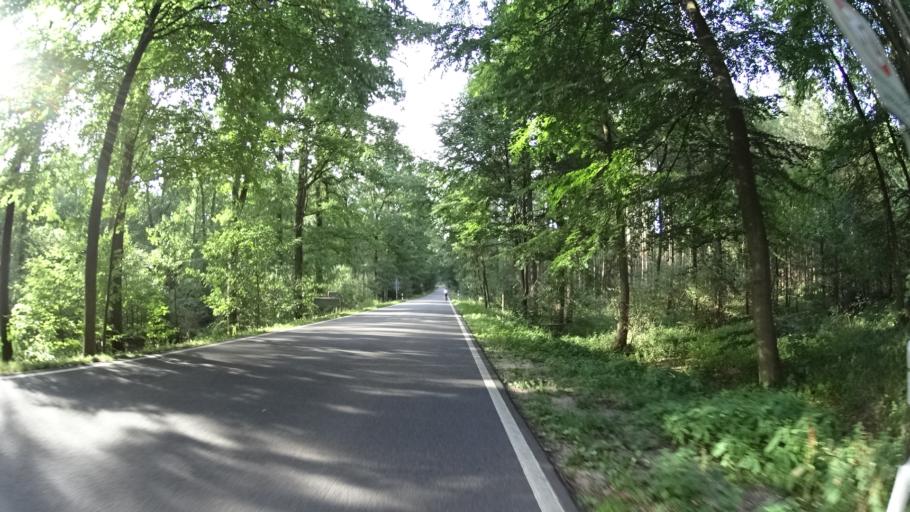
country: DE
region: Lower Saxony
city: Undeloh
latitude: 53.1657
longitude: 9.8952
